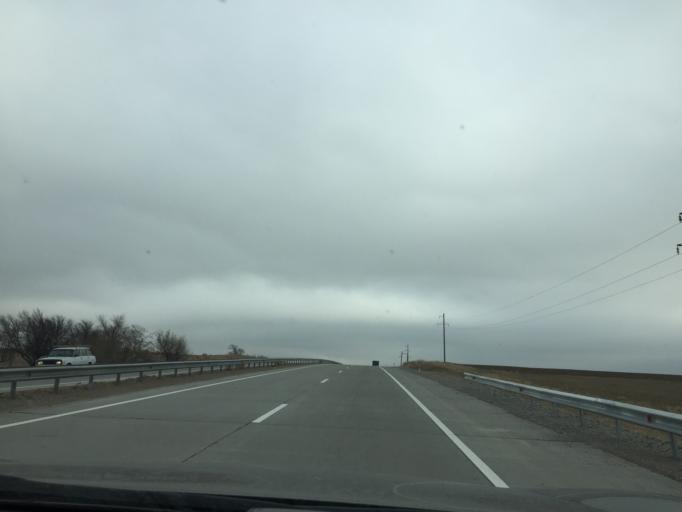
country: KZ
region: Ongtustik Qazaqstan
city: Sastobe
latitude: 42.5536
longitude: 70.1215
